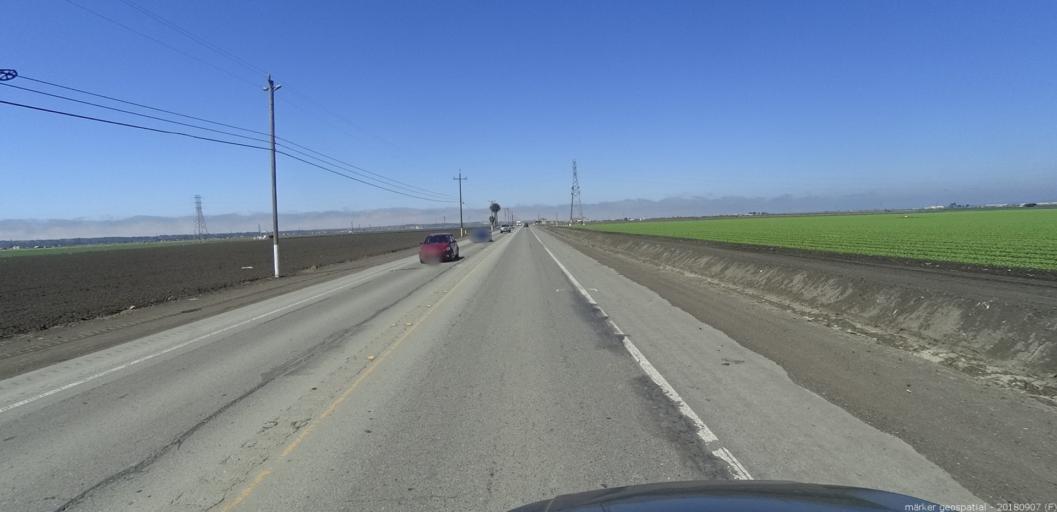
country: US
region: California
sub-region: Monterey County
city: Boronda
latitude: 36.6725
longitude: -121.6952
